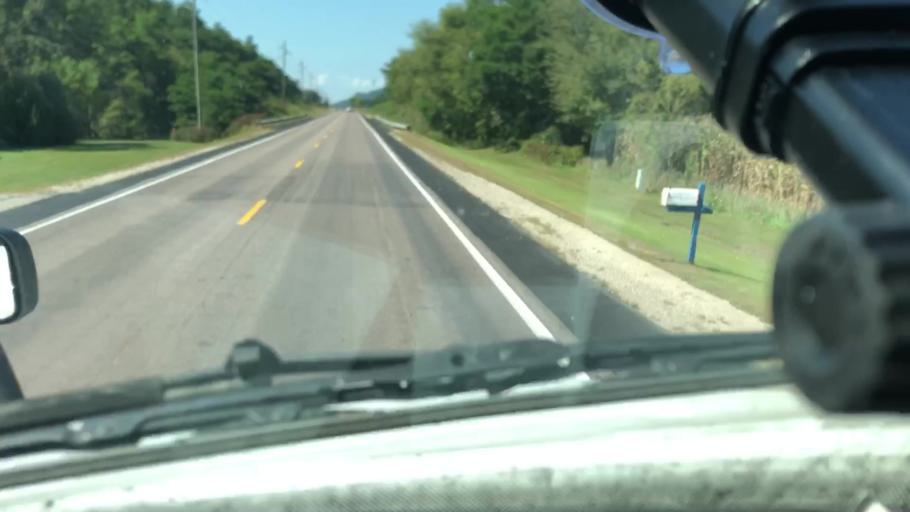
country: US
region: Wisconsin
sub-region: Trempealeau County
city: Trempealeau
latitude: 44.0700
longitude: -91.4996
